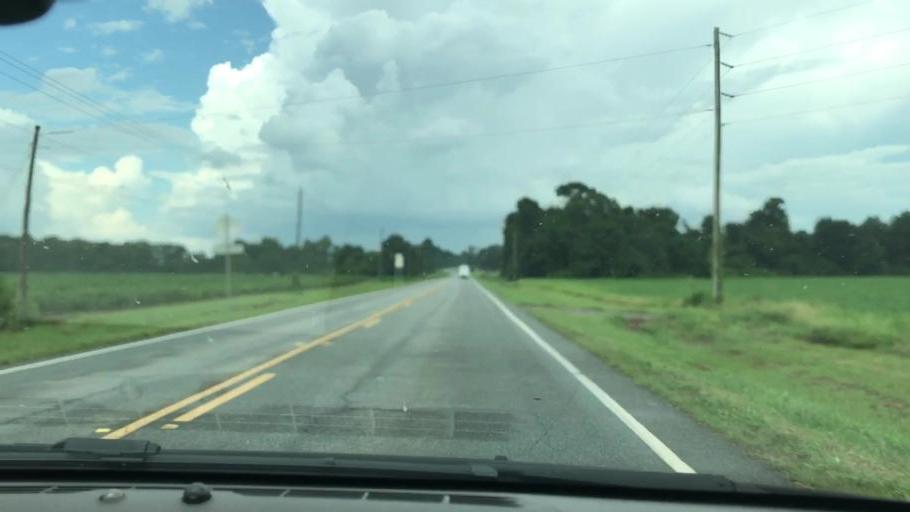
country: US
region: Georgia
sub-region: Early County
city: Blakely
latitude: 31.3756
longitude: -84.9575
